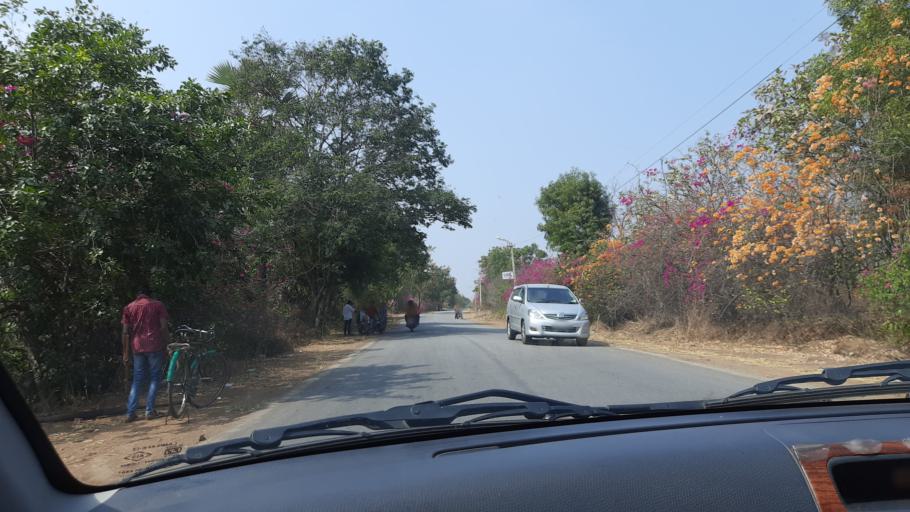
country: IN
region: Telangana
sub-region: Rangareddi
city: Lal Bahadur Nagar
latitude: 17.2774
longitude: 78.6561
